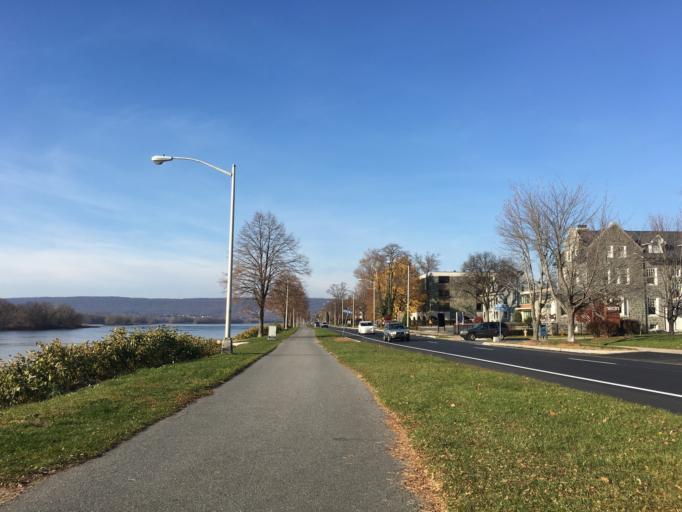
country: US
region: Pennsylvania
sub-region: Dauphin County
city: Harrisburg
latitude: 40.2720
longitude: -76.8957
